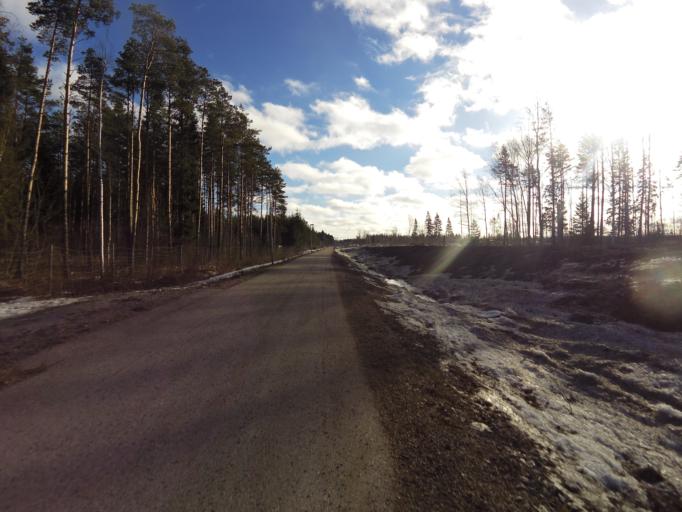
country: SE
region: Gaevleborg
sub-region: Gavle Kommun
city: Gavle
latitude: 60.6482
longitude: 17.2486
